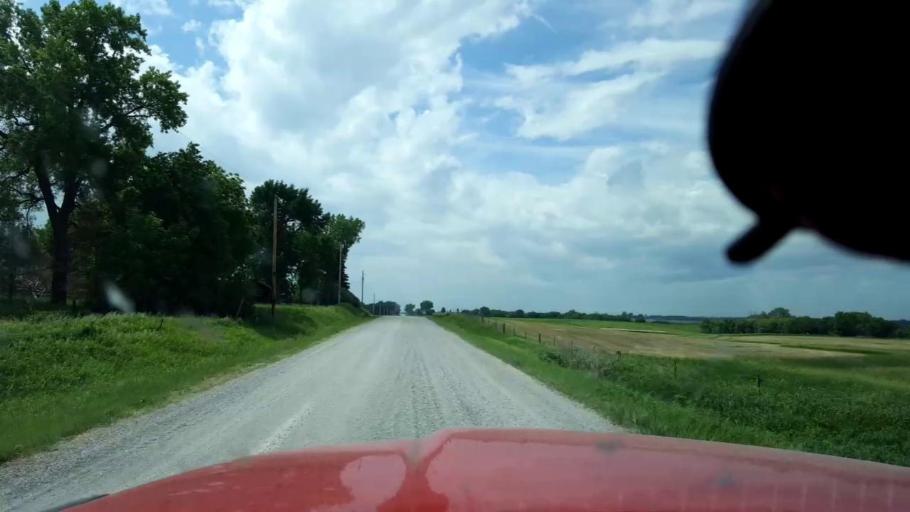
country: US
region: Iowa
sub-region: Cherokee County
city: Cherokee
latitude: 42.8187
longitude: -95.5343
